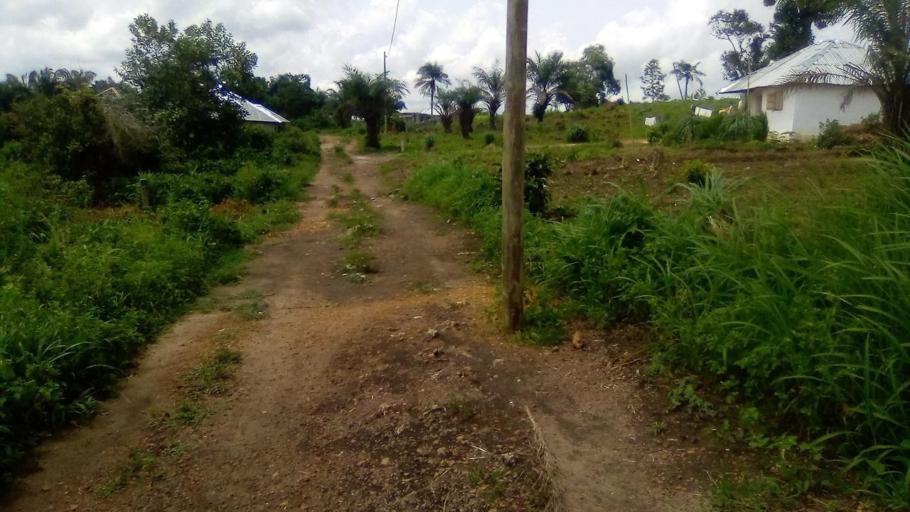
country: SL
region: Southern Province
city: Bo
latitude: 7.9306
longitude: -11.7470
